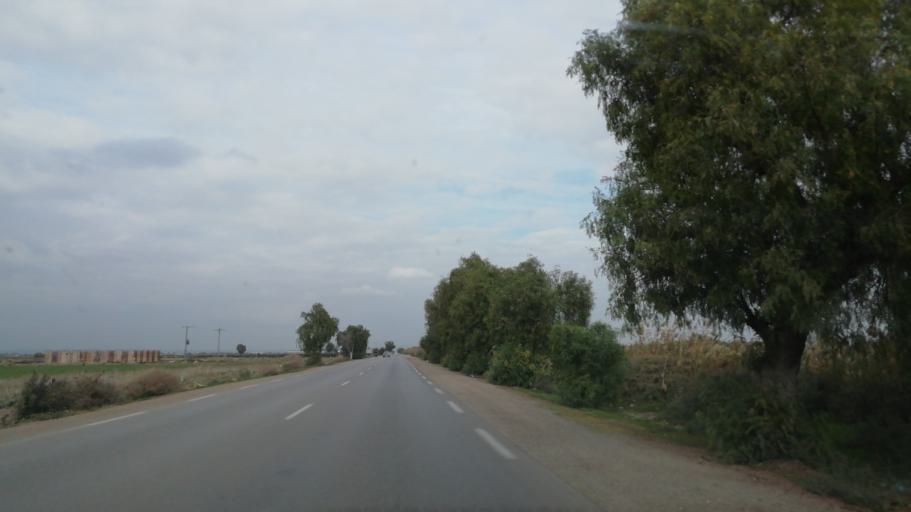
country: DZ
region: Mascara
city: Mascara
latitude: 35.6394
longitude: 0.0605
